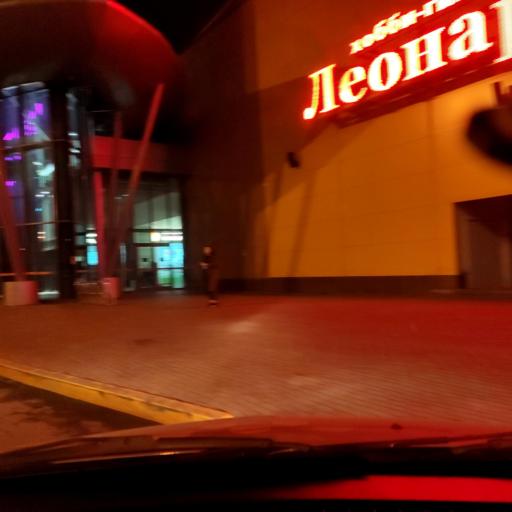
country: RU
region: Bashkortostan
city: Ufa
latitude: 54.7574
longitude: 56.0338
